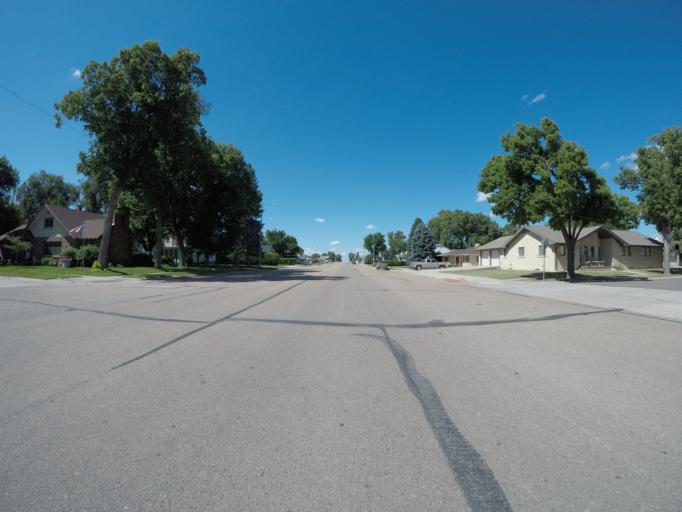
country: US
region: Nebraska
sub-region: Chase County
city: Imperial
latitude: 40.5209
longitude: -101.6431
